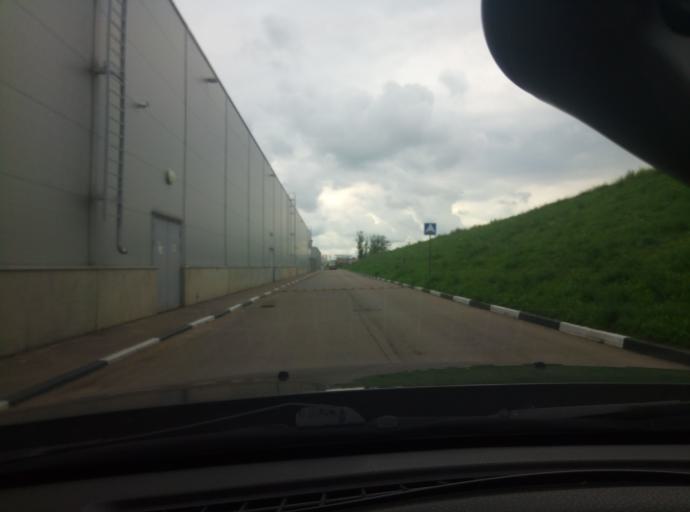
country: RU
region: Tula
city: Tula
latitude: 54.1729
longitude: 37.6427
